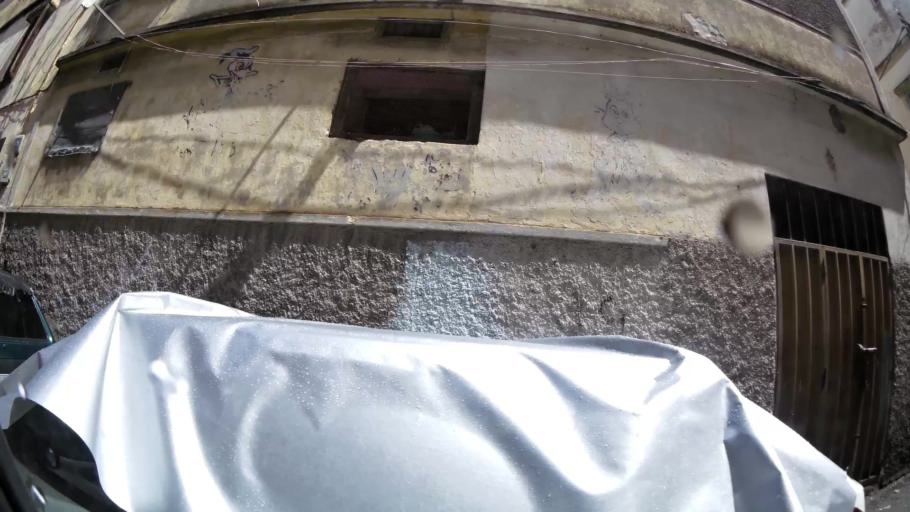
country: MA
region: Grand Casablanca
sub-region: Casablanca
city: Casablanca
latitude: 33.5762
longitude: -7.5921
